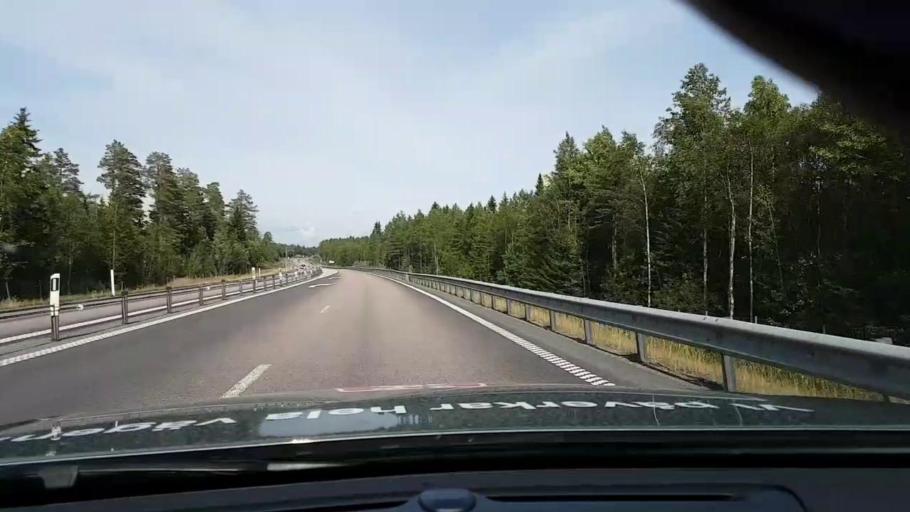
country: SE
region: Vaesternorrland
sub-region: OErnskoeldsviks Kommun
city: Husum
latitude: 63.3712
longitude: 19.1893
